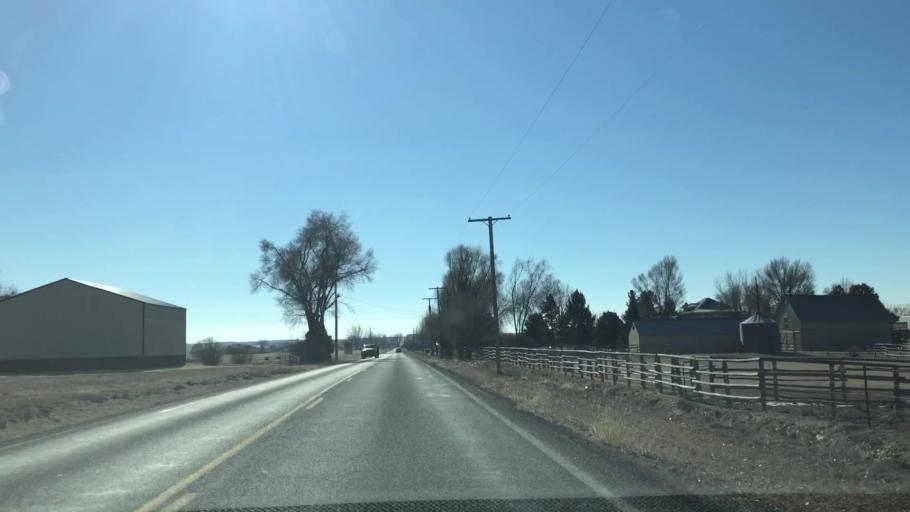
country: US
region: Colorado
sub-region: Weld County
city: Windsor
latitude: 40.4991
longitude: -104.9442
